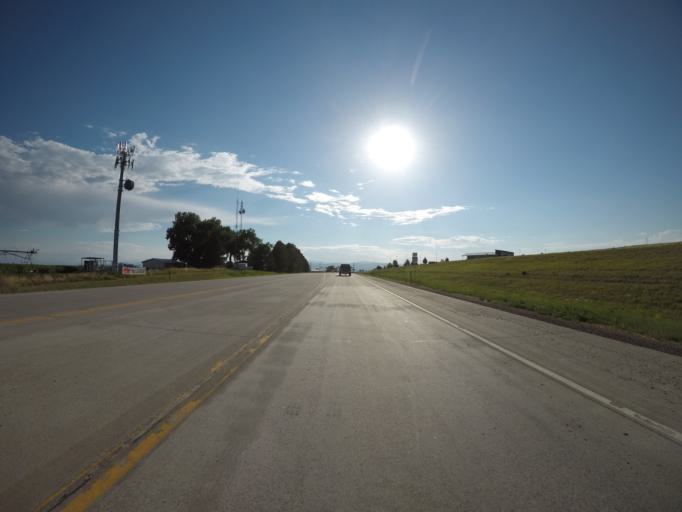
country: US
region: Colorado
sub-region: Weld County
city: Severance
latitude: 40.5816
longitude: -104.9040
